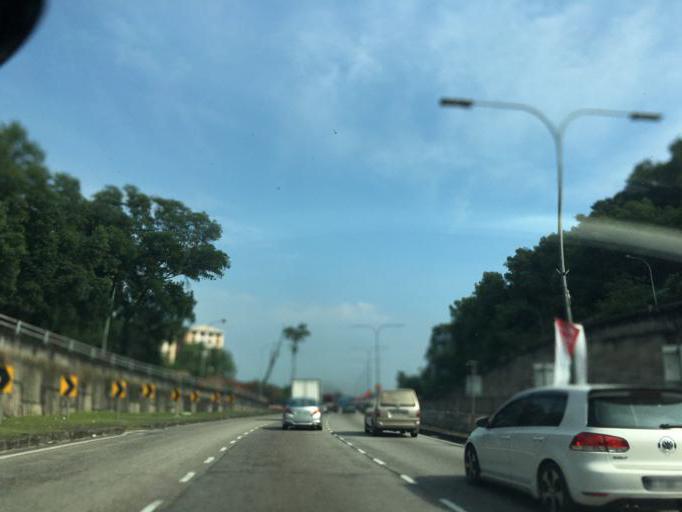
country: MY
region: Kuala Lumpur
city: Kuala Lumpur
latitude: 3.2266
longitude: 101.7275
